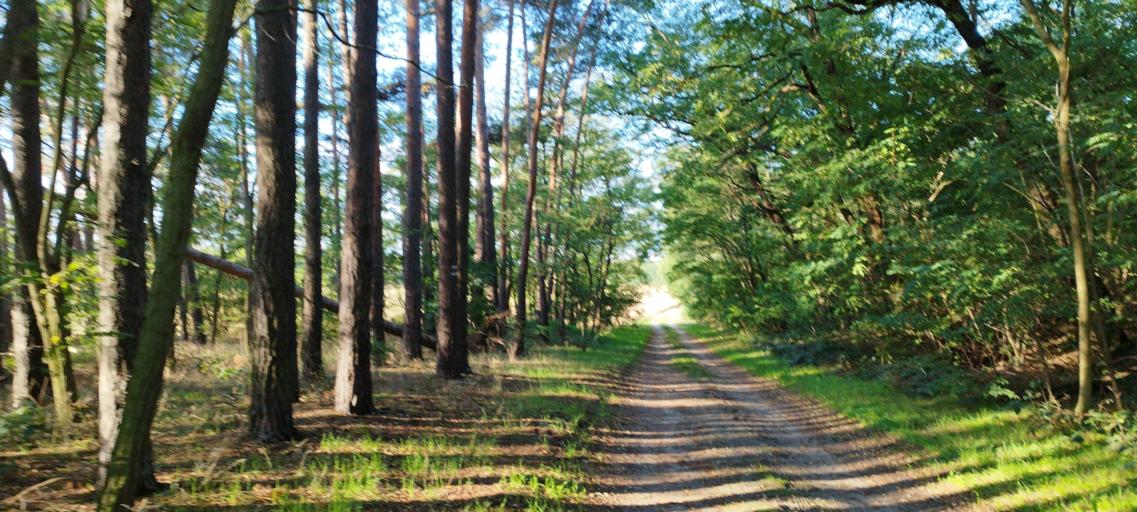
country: DE
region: Brandenburg
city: Neuzelle
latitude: 52.0861
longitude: 14.6311
